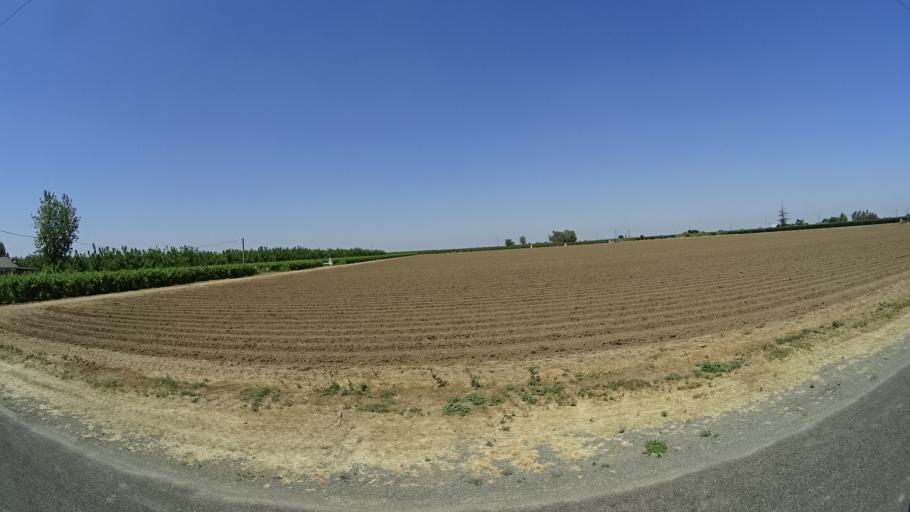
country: US
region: California
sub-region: Fresno County
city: Kingsburg
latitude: 36.4707
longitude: -119.5821
